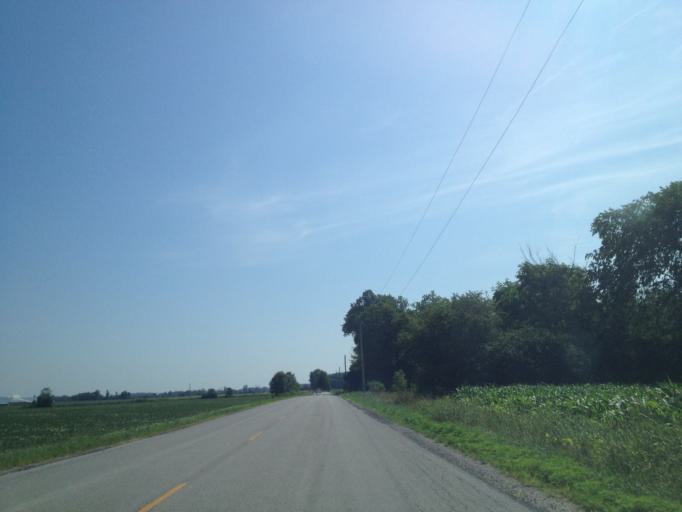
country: CA
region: Ontario
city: London
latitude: 43.1287
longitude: -81.2118
